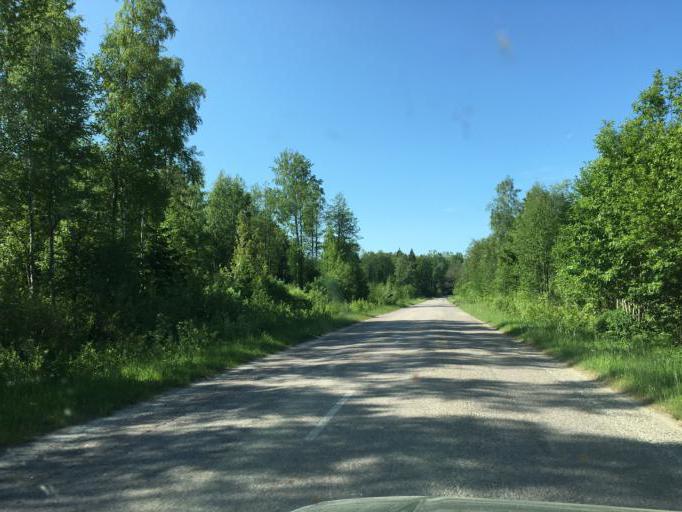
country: LV
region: Ventspils
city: Ventspils
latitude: 57.4953
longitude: 21.8116
